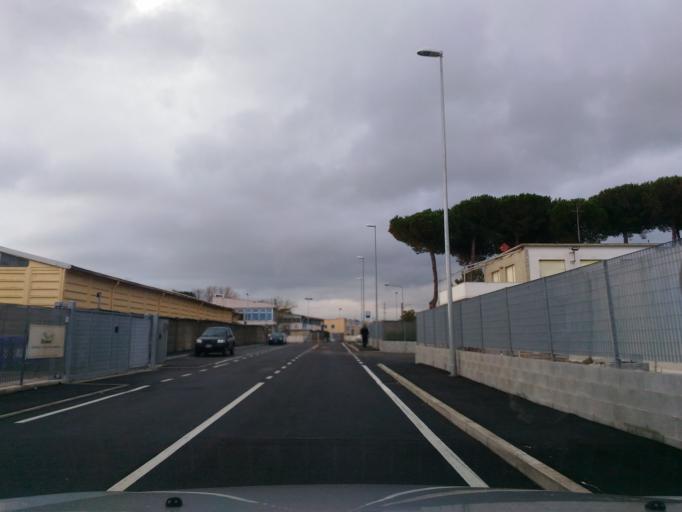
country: IT
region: Tuscany
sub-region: Provincia di Livorno
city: Livorno
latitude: 43.5644
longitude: 10.3374
